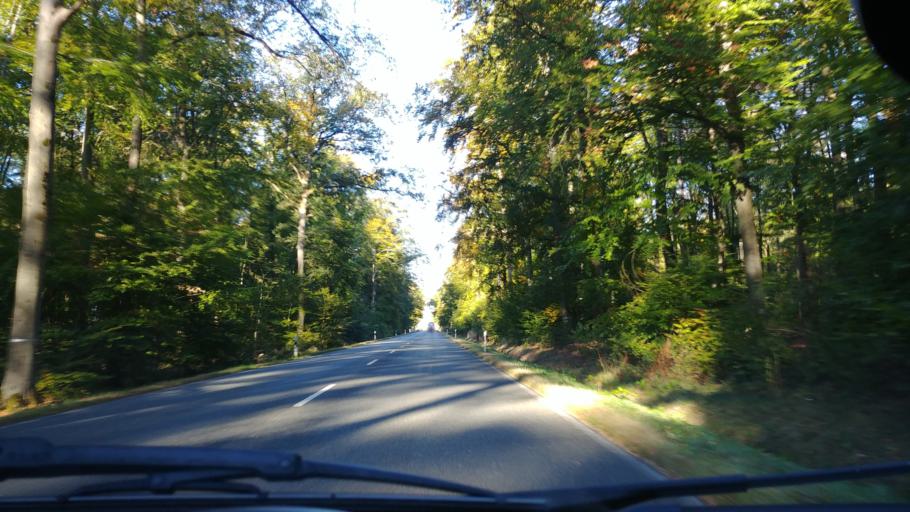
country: DE
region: Rheinland-Pfalz
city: Holzhausen an der Haide
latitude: 50.2097
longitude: 7.9279
